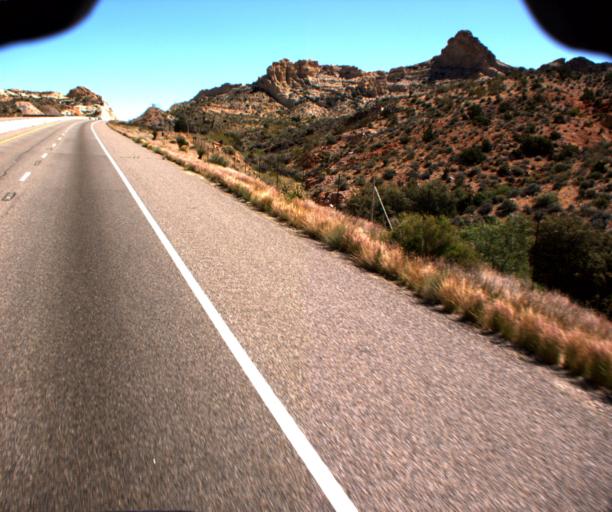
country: US
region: Arizona
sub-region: Mohave County
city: Golden Valley
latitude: 35.2149
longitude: -114.3965
